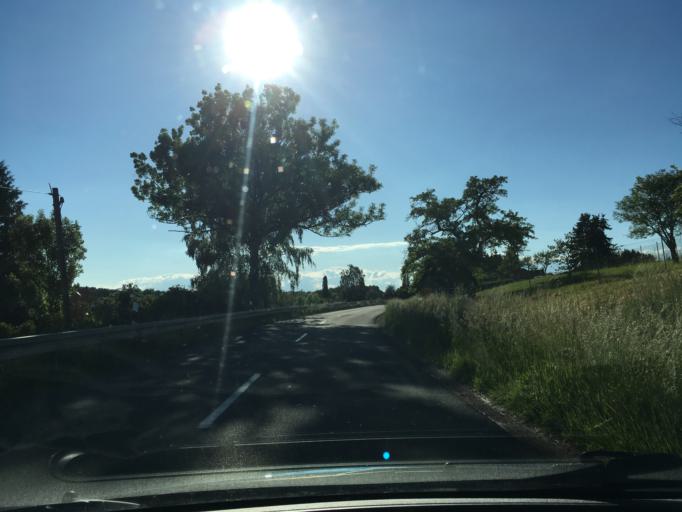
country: DE
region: Lower Saxony
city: Coppengrave
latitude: 51.9875
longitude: 9.7283
